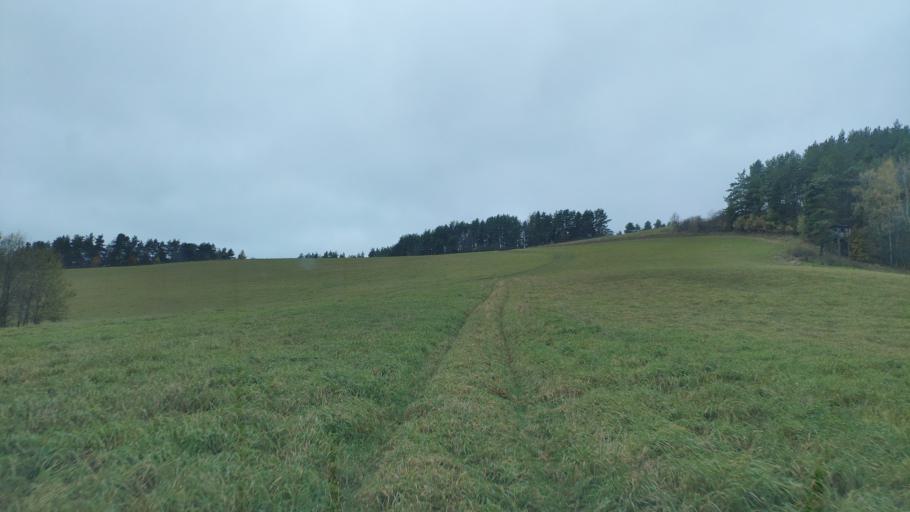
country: SK
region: Presovsky
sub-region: Okres Presov
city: Presov
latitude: 48.9346
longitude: 21.1142
